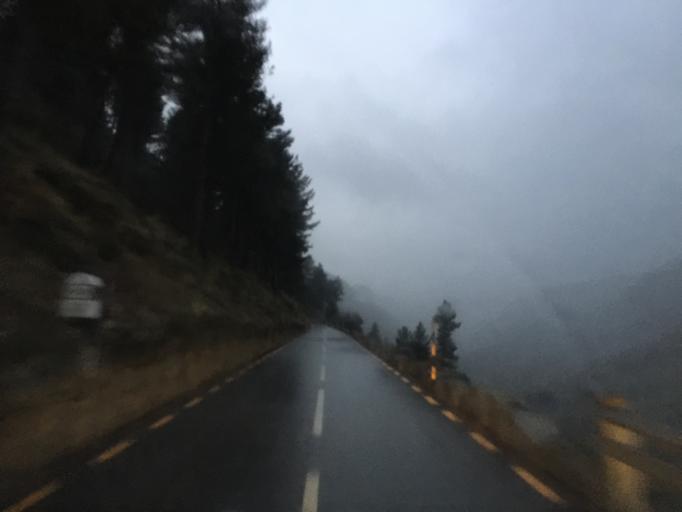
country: PT
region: Guarda
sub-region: Manteigas
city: Manteigas
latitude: 40.3525
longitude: -7.5593
